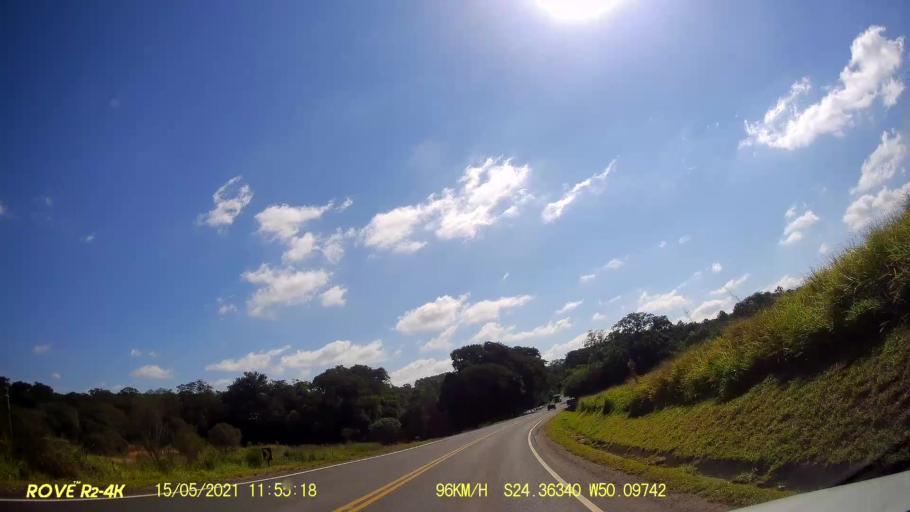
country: BR
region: Parana
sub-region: Pirai Do Sul
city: Pirai do Sul
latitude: -24.3635
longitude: -50.0972
